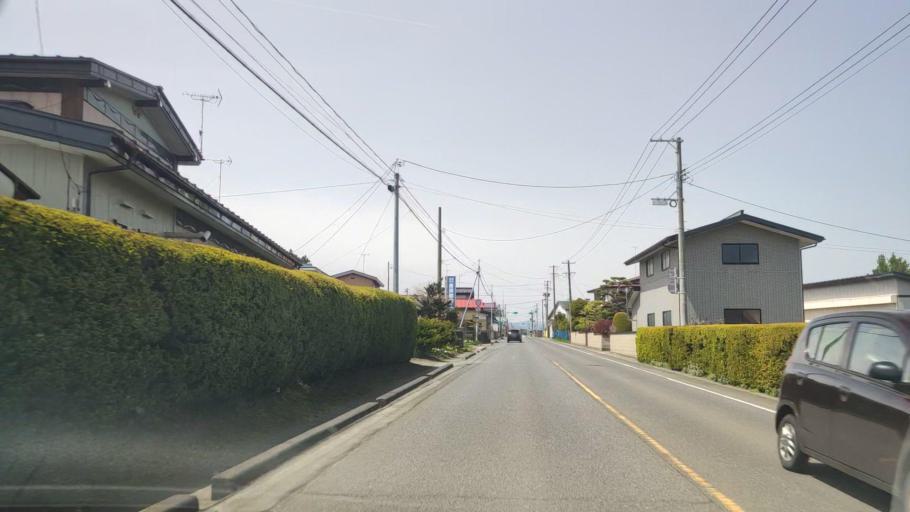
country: JP
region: Aomori
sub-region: Misawa Shi
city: Inuotose
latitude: 40.6013
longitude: 141.3046
